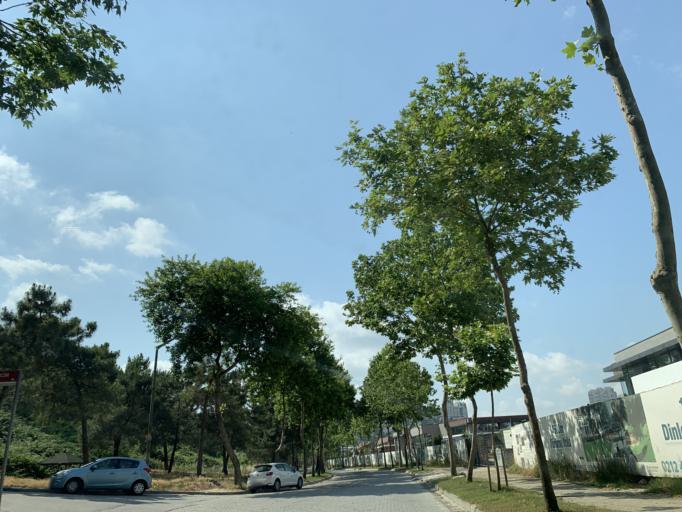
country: TR
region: Istanbul
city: Esenyurt
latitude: 41.0640
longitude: 28.6963
